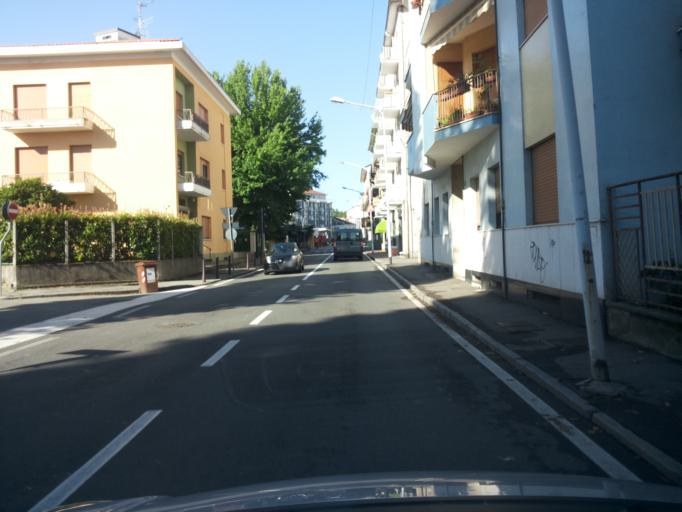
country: IT
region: Piedmont
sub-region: Provincia di Torino
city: Ivrea
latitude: 45.4698
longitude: 7.8872
